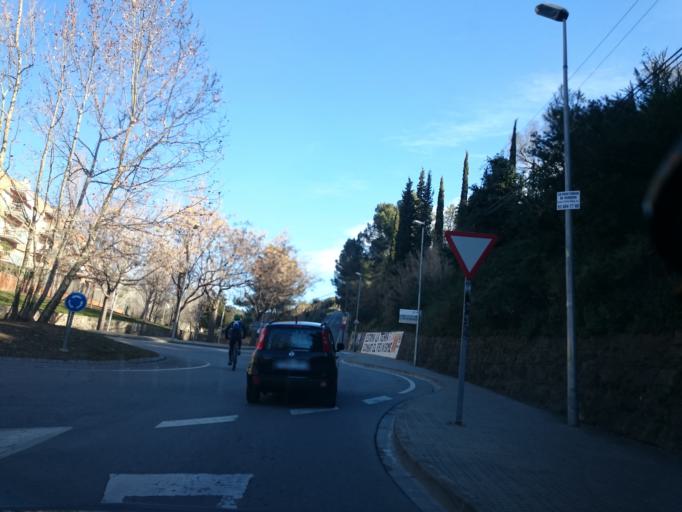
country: ES
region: Catalonia
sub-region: Provincia de Barcelona
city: Molins de Rei
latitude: 41.4167
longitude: 2.0228
